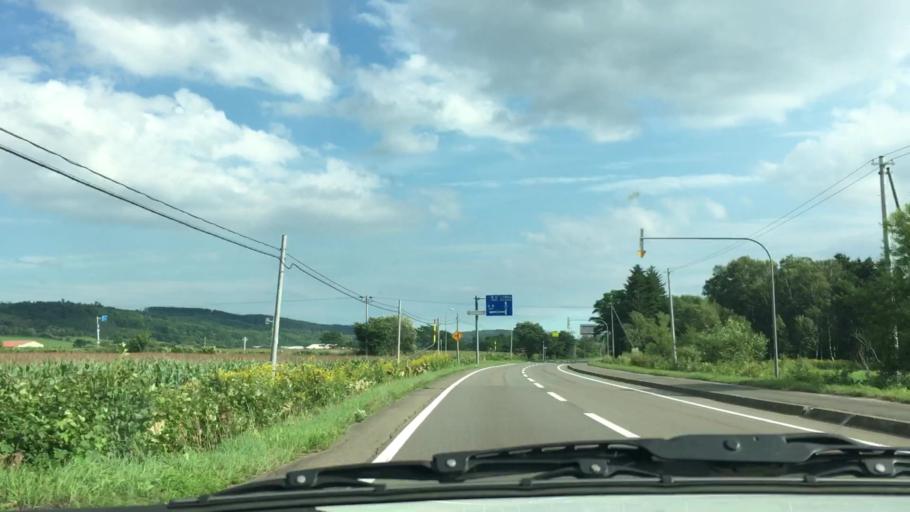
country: JP
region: Hokkaido
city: Otofuke
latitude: 43.3250
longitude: 143.2992
